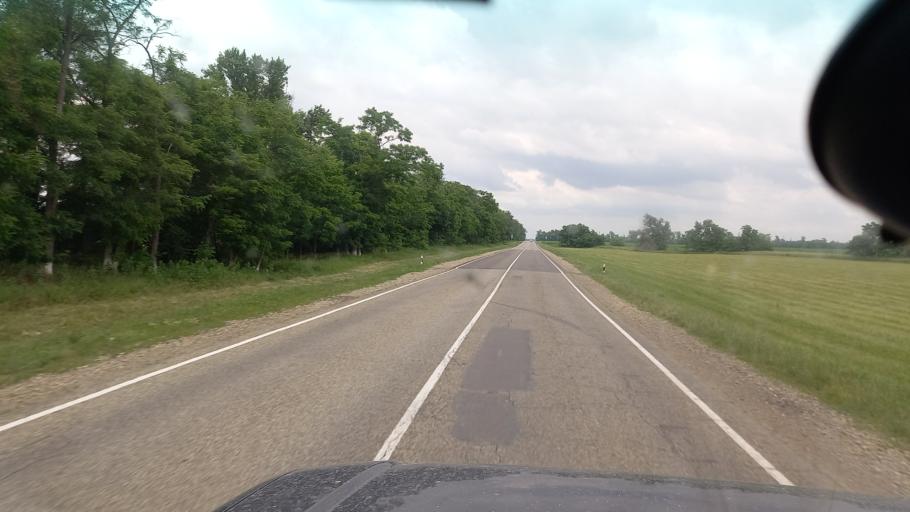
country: RU
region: Adygeya
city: Blechepsin
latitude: 44.8433
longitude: 40.4986
